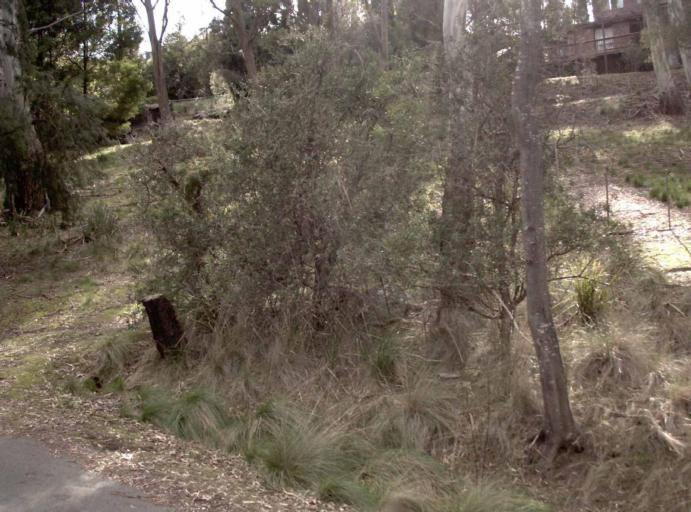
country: AU
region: Tasmania
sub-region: Launceston
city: West Launceston
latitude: -41.4410
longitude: 147.1148
